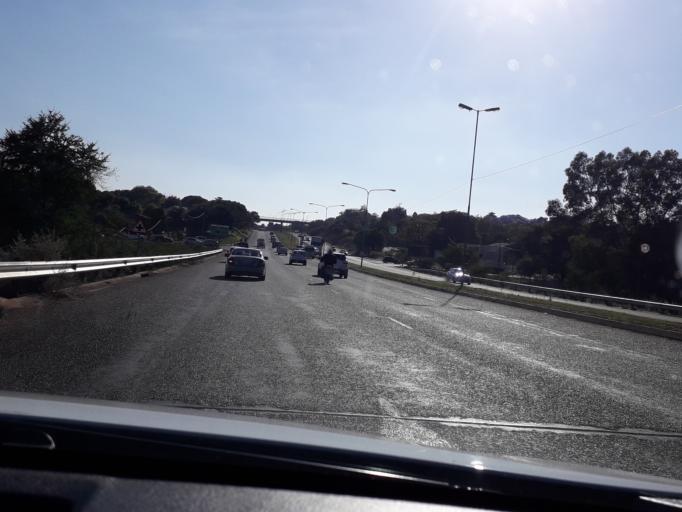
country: ZA
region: Gauteng
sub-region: City of Tshwane Metropolitan Municipality
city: Centurion
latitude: -25.8174
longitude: 28.2035
